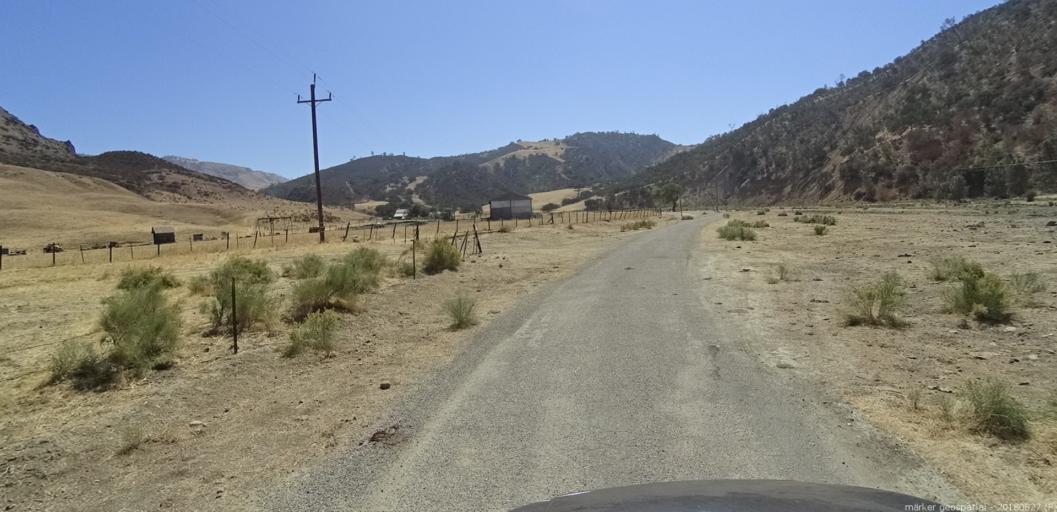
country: US
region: California
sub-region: Monterey County
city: King City
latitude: 36.2934
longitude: -120.8925
